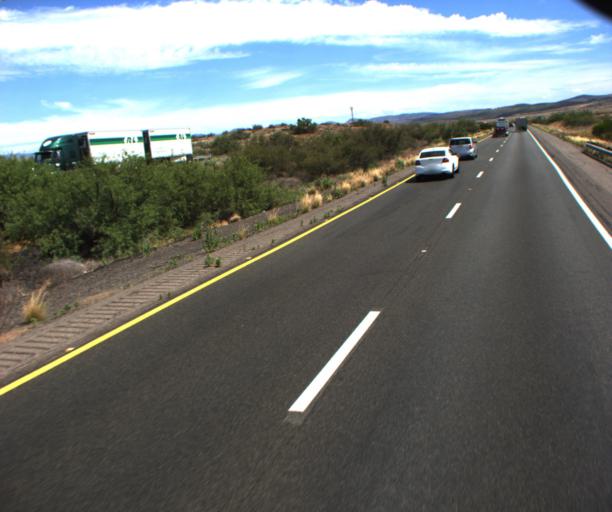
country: US
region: Arizona
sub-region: Yavapai County
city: Cordes Lakes
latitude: 34.3950
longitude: -112.0800
